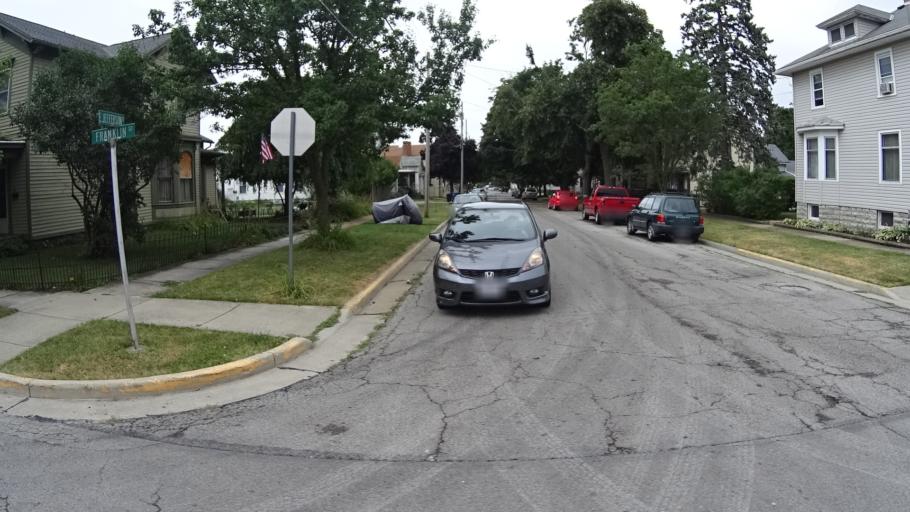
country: US
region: Ohio
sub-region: Erie County
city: Sandusky
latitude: 41.4541
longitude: -82.7048
